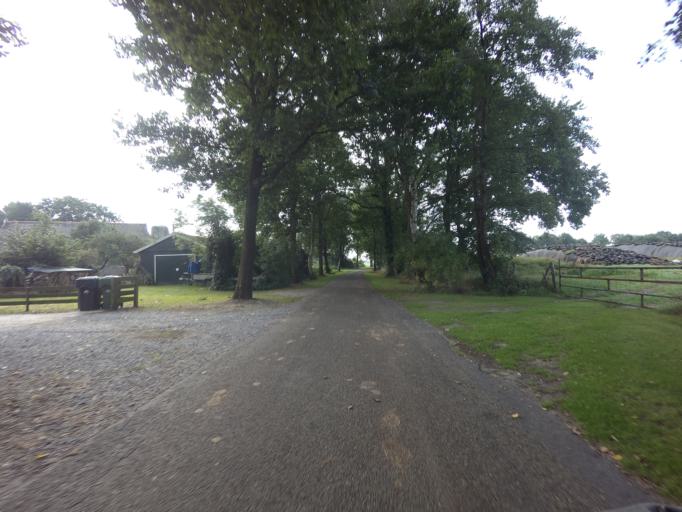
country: NL
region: Friesland
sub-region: Gemeente Weststellingwerf
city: Noordwolde
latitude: 52.9551
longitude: 6.2230
